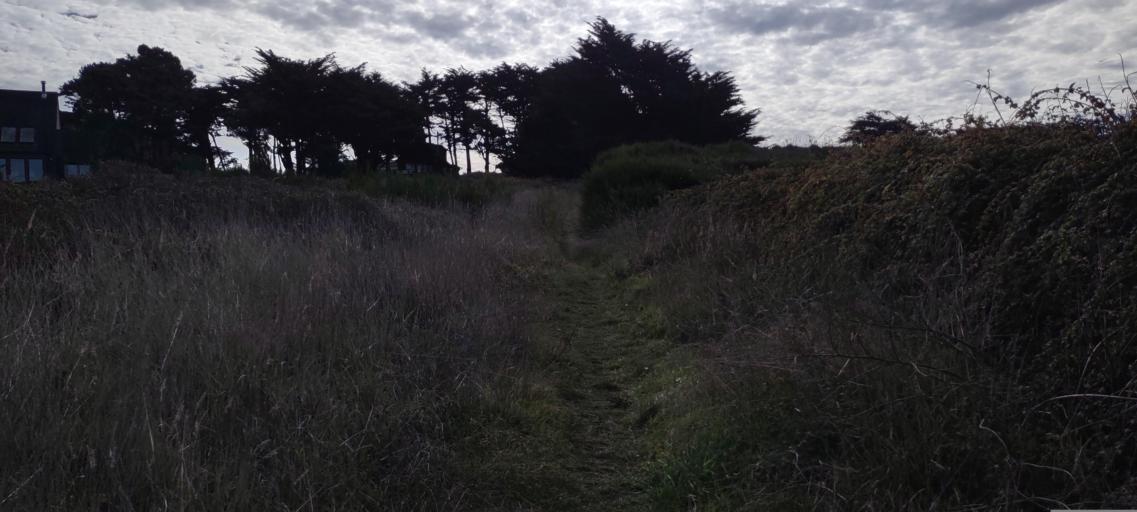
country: US
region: California
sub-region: Mendocino County
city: Fort Bragg
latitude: 39.3113
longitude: -123.8034
